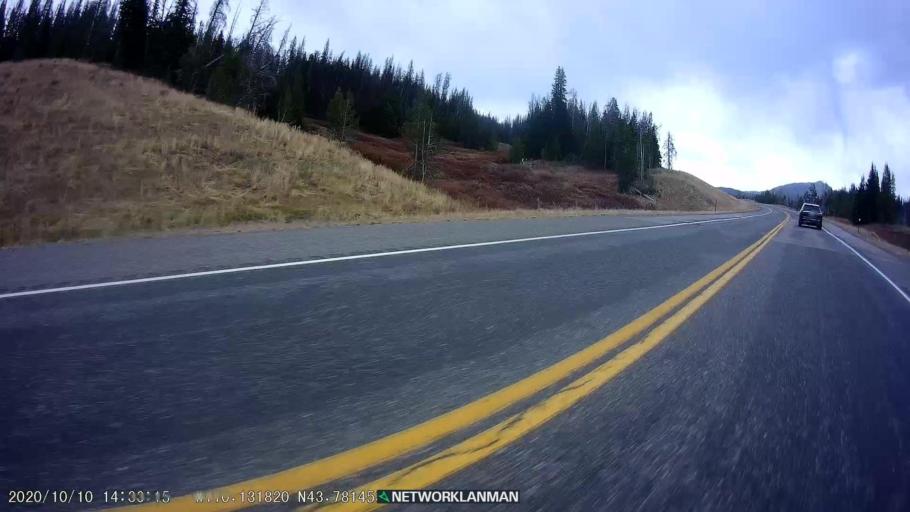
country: US
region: Wyoming
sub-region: Teton County
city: Jackson
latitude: 43.7813
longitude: -110.1316
